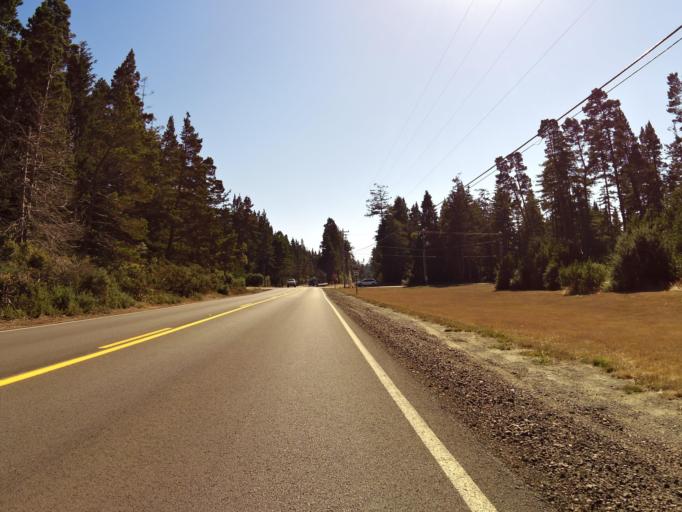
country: US
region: Oregon
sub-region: Coos County
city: Bandon
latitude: 43.1881
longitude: -124.3677
